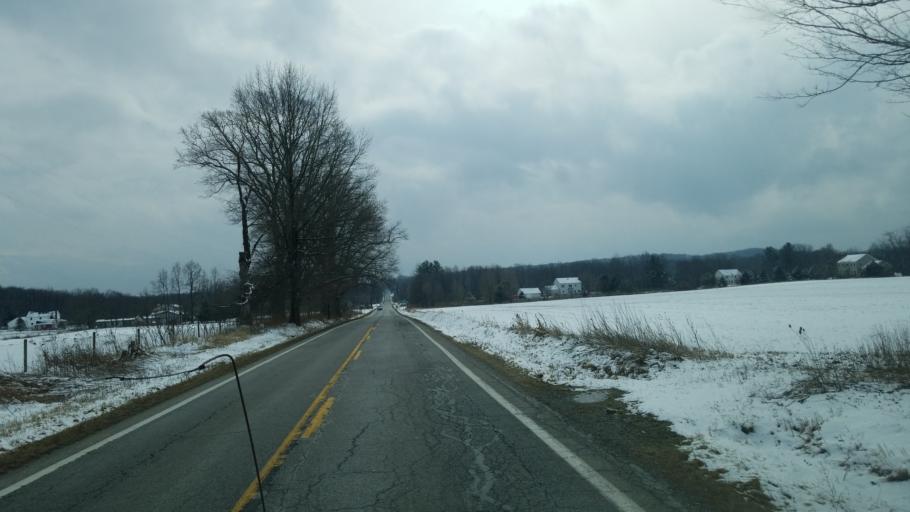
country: US
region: Ohio
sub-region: Portage County
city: Hiram
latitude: 41.3497
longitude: -81.1432
